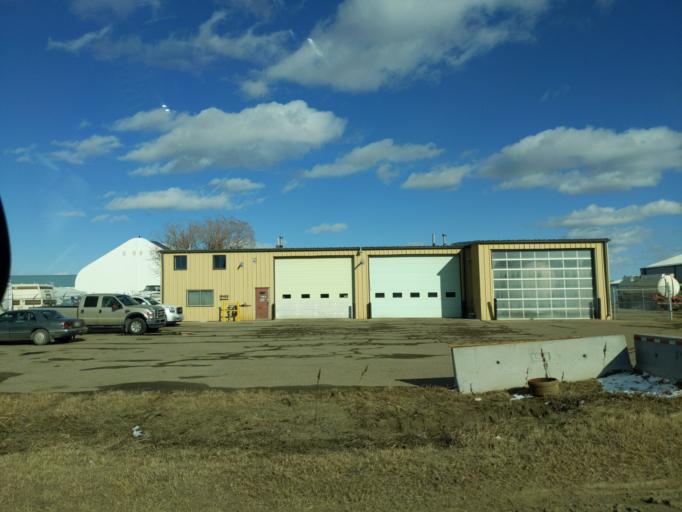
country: CA
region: Saskatchewan
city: Lloydminster
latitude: 53.2764
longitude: -109.9703
